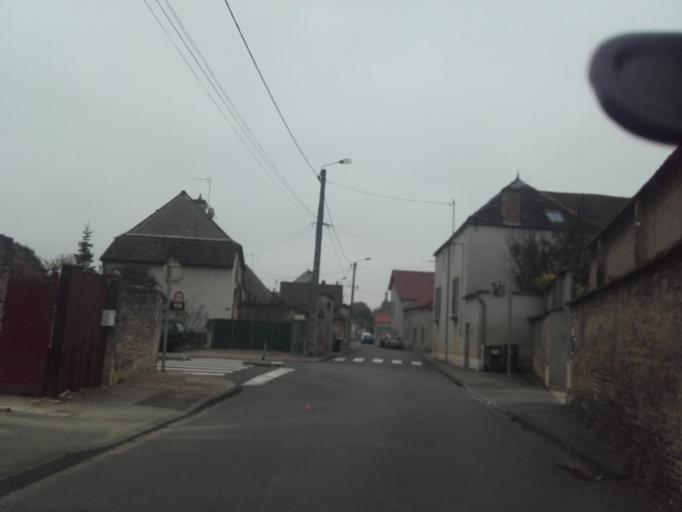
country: FR
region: Bourgogne
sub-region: Departement de la Cote-d'Or
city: Beaune
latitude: 47.0279
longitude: 4.8298
